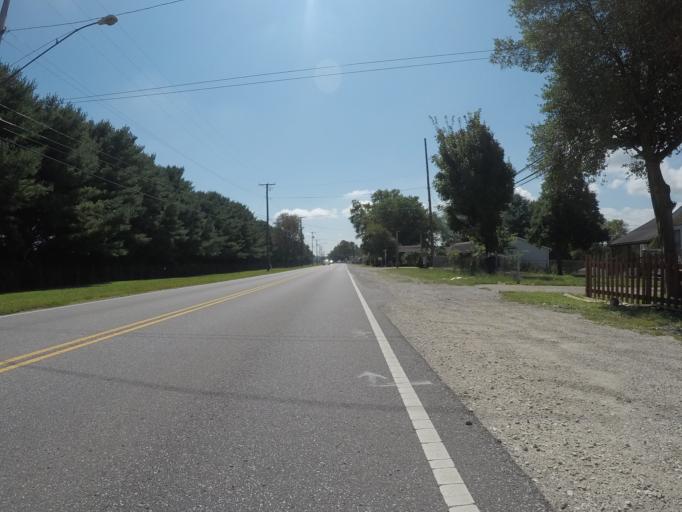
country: US
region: Ohio
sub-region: Lawrence County
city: South Point
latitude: 38.4290
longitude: -82.5932
